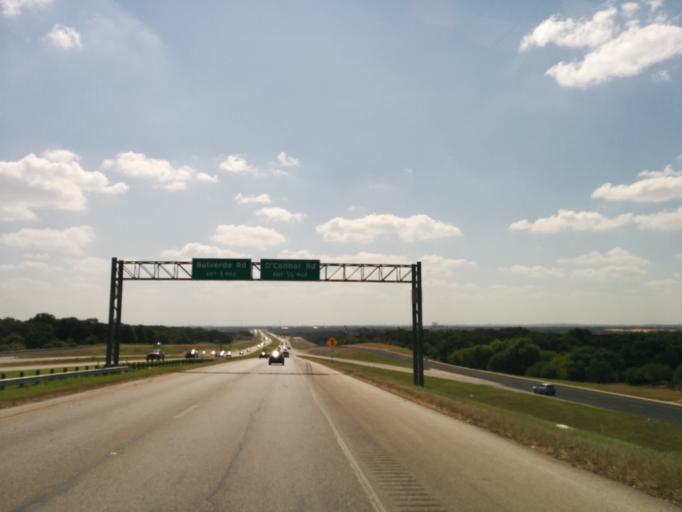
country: US
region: Texas
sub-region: Bexar County
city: Live Oak
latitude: 29.6025
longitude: -98.3898
